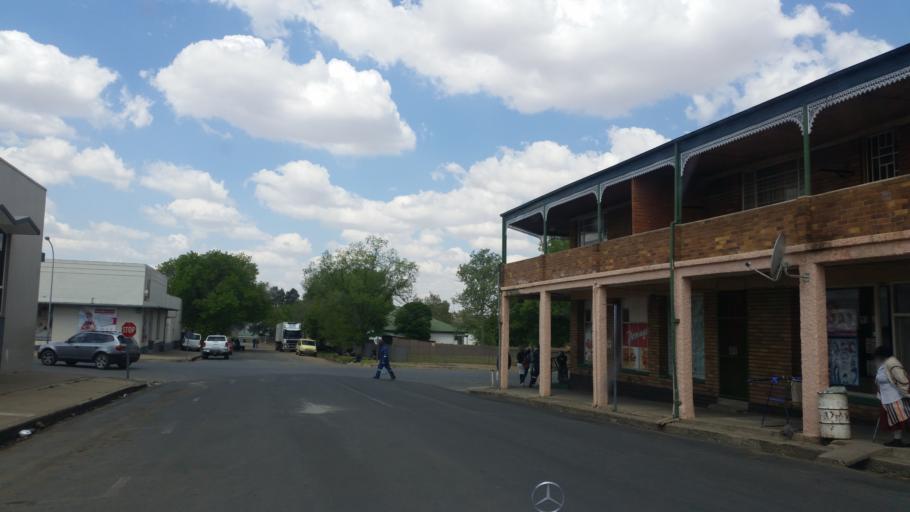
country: ZA
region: Orange Free State
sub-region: Thabo Mofutsanyana District Municipality
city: Reitz
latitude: -27.7983
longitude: 28.4309
